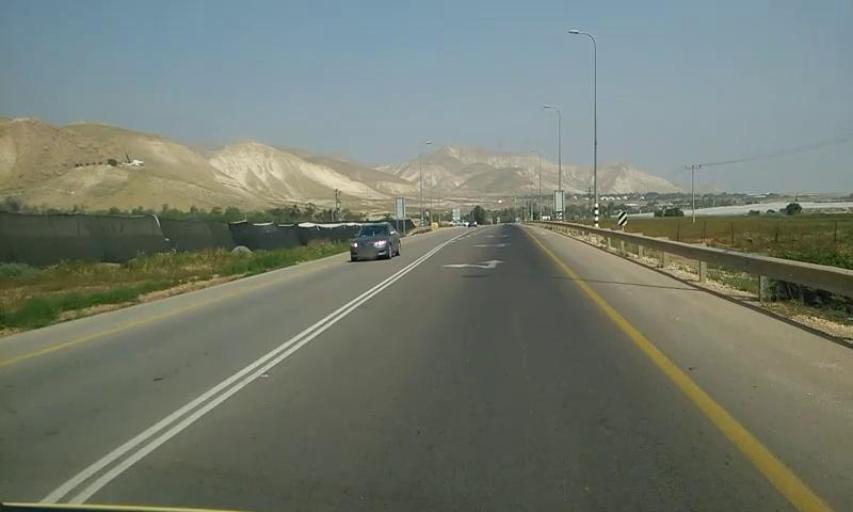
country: PS
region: West Bank
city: Al Fasayil
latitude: 32.0472
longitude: 35.4633
